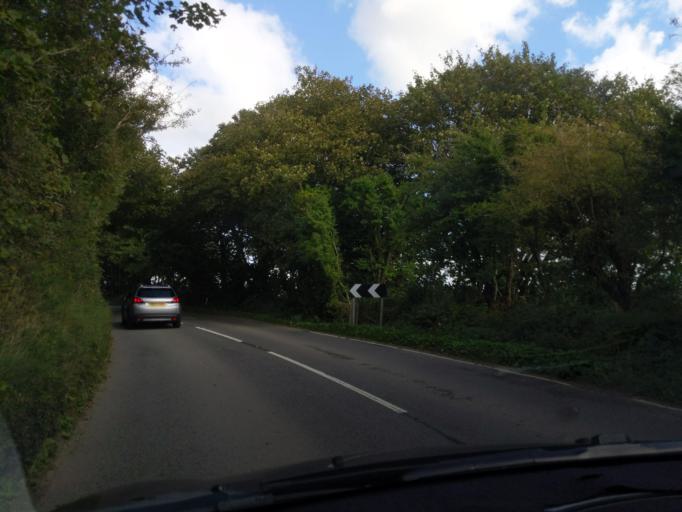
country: GB
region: England
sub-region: Devon
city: Holsworthy
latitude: 50.8485
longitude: -4.3385
